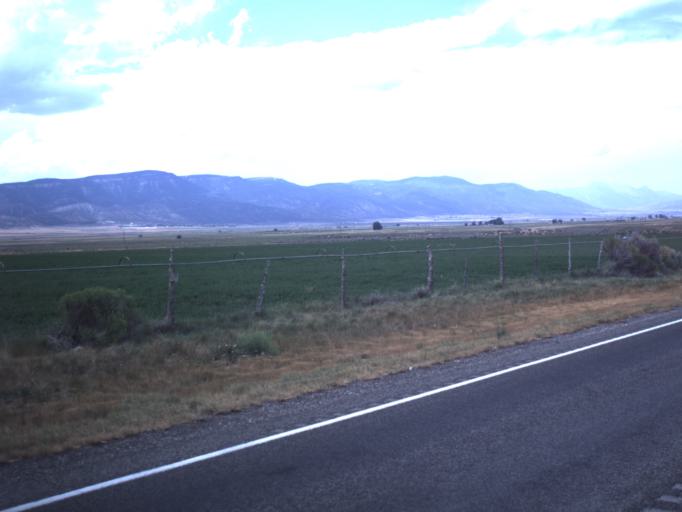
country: US
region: Utah
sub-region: Sanpete County
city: Ephraim
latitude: 39.4322
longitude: -111.5623
